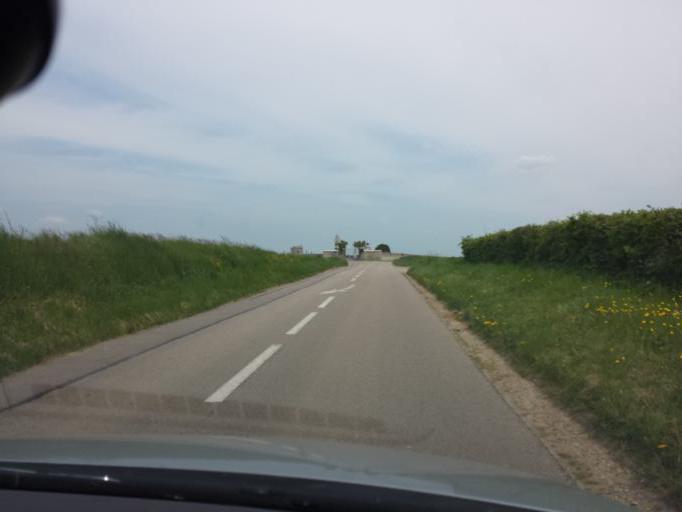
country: FR
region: Ile-de-France
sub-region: Departement des Yvelines
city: Tacoignieres
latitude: 48.8681
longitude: 1.6216
